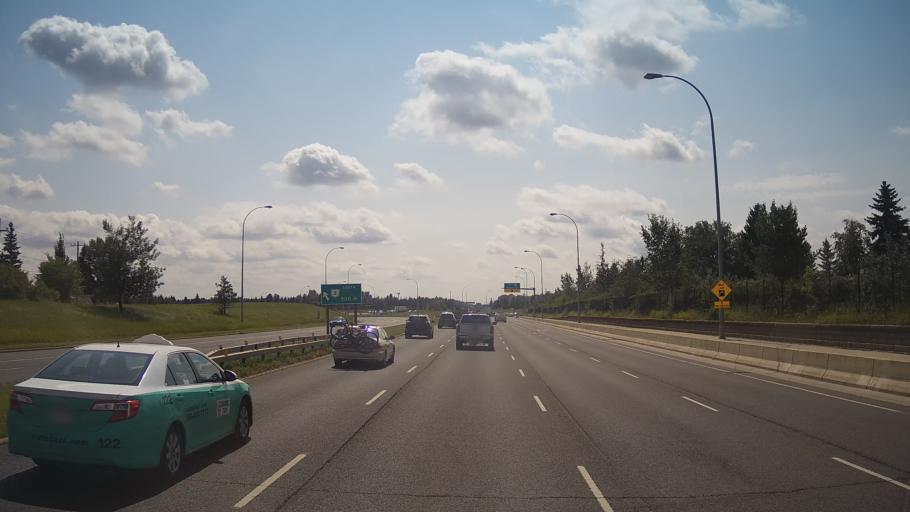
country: CA
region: Alberta
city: St. Albert
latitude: 53.5161
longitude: -113.6154
